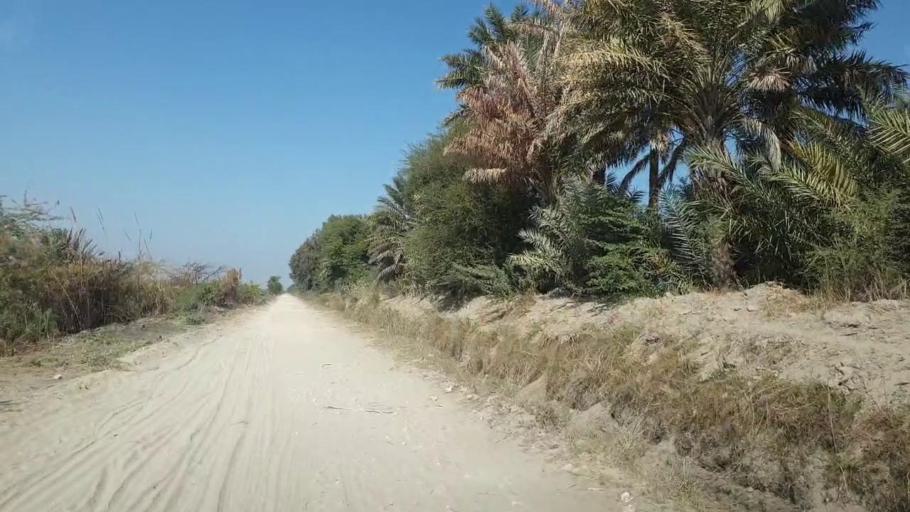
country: PK
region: Sindh
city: Mirpur Khas
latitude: 25.6518
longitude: 69.0274
